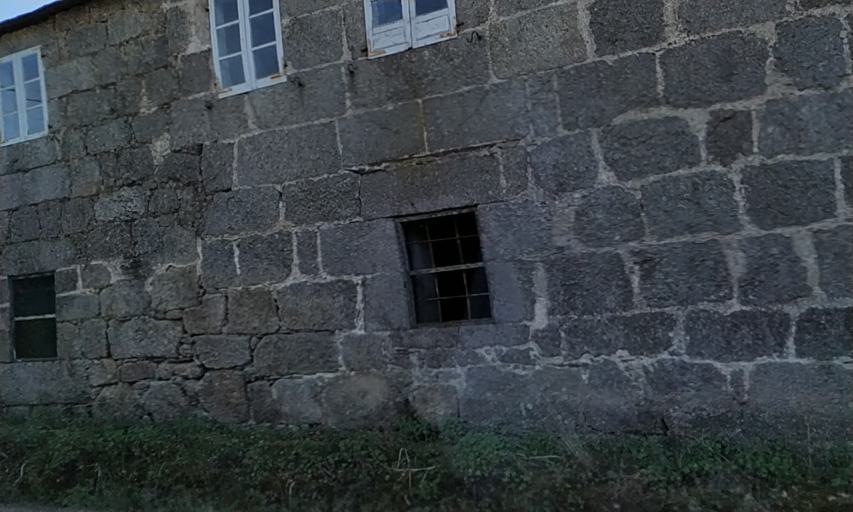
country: ES
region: Galicia
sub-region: Provincia de Lugo
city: Corgo
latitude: 42.9547
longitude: -7.4650
